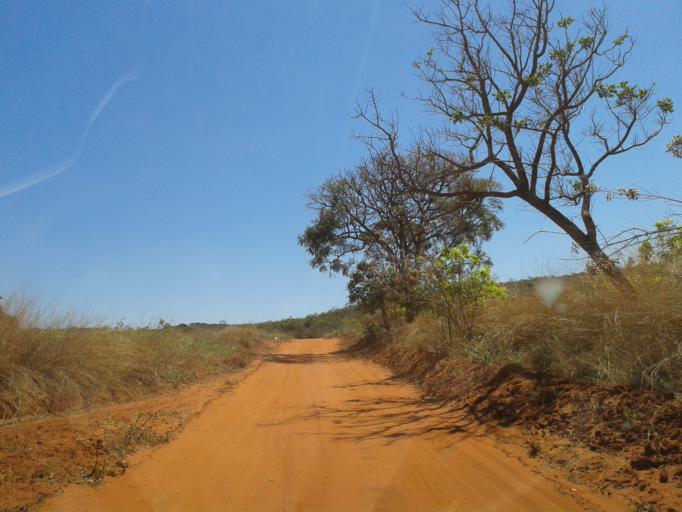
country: BR
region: Minas Gerais
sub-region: Ituiutaba
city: Ituiutaba
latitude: -19.1006
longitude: -49.2945
